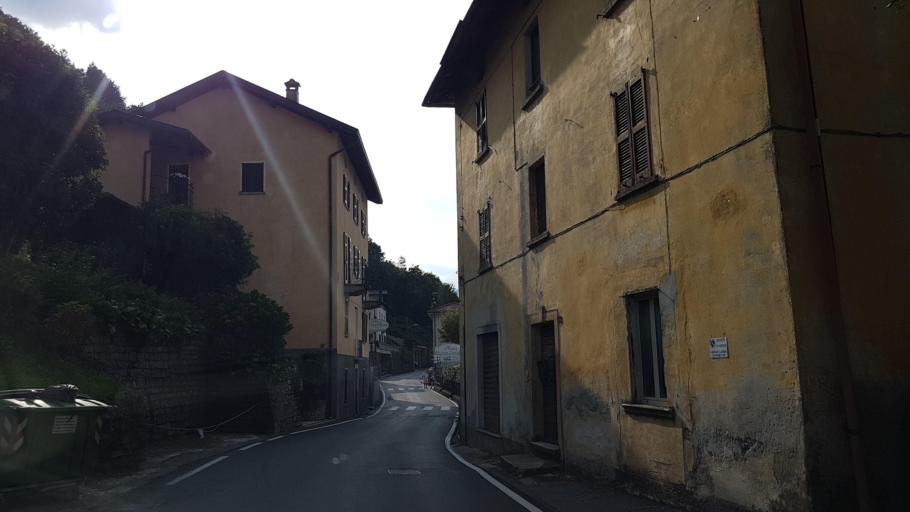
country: IT
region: Lombardy
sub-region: Provincia di Como
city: Lezzeno
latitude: 45.9466
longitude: 9.2016
